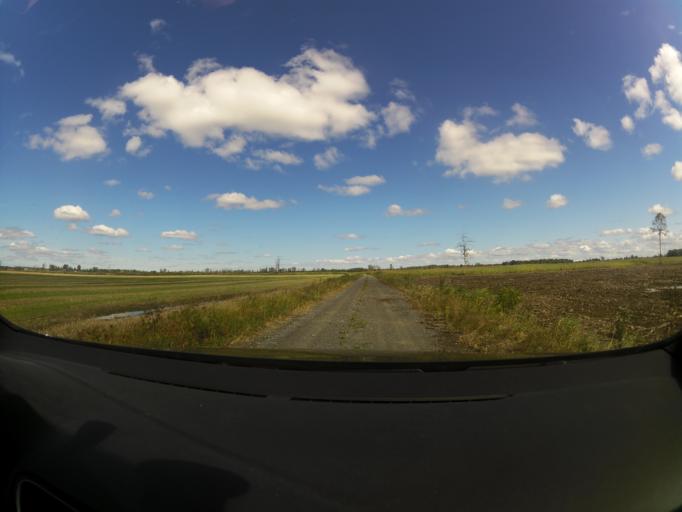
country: CA
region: Ontario
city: Carleton Place
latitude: 45.1655
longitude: -76.0953
